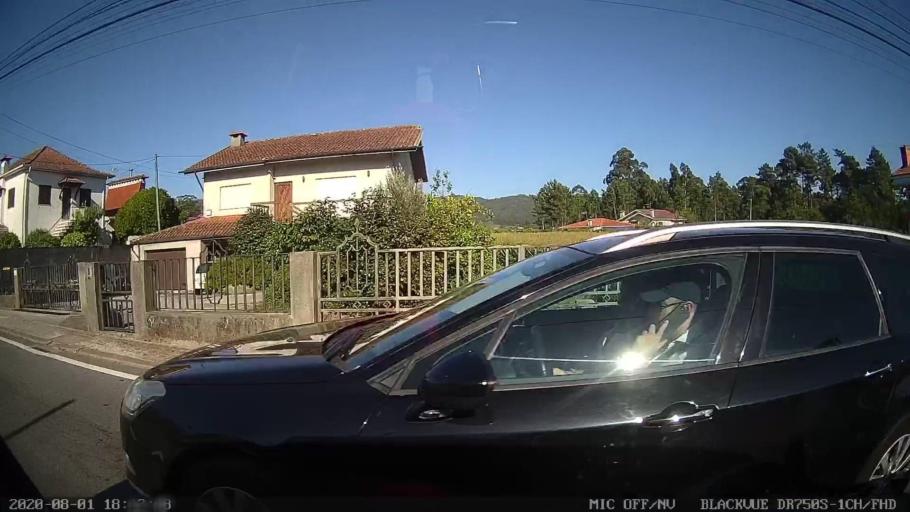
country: PT
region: Porto
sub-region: Santo Tirso
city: Sao Miguel do Couto
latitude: 41.2875
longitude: -8.4718
